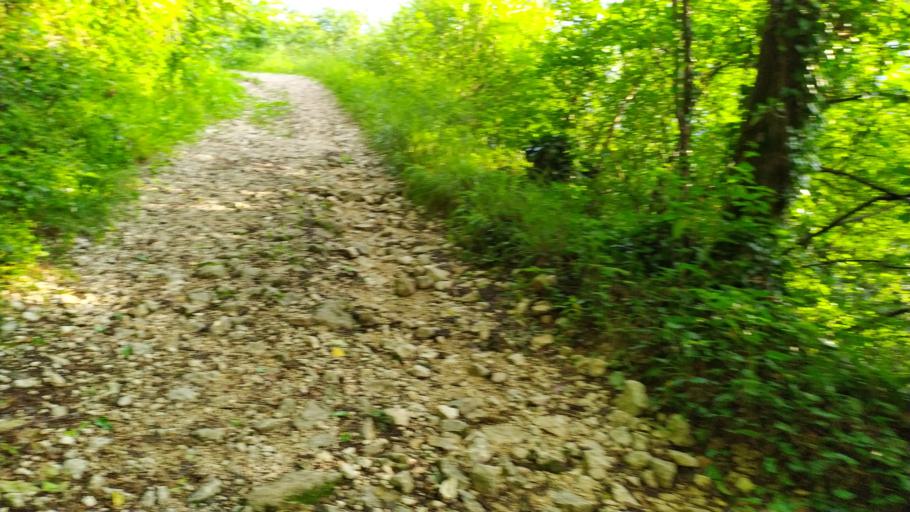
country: IT
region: Veneto
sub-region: Provincia di Vicenza
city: San Quirico
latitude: 45.6833
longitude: 11.2772
